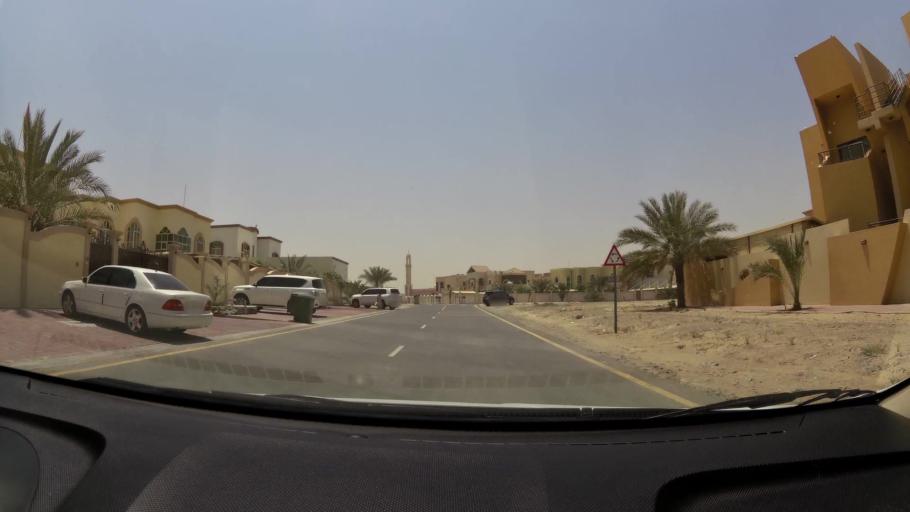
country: AE
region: Ajman
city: Ajman
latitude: 25.4064
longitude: 55.5214
